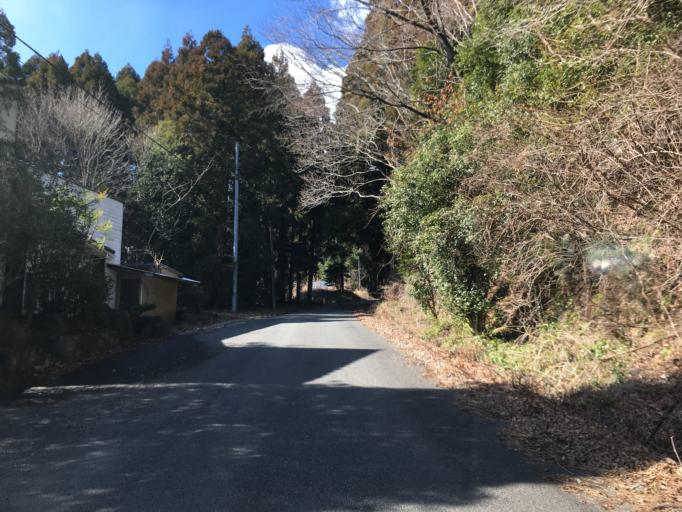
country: JP
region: Fukushima
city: Iwaki
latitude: 37.0137
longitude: 140.7870
